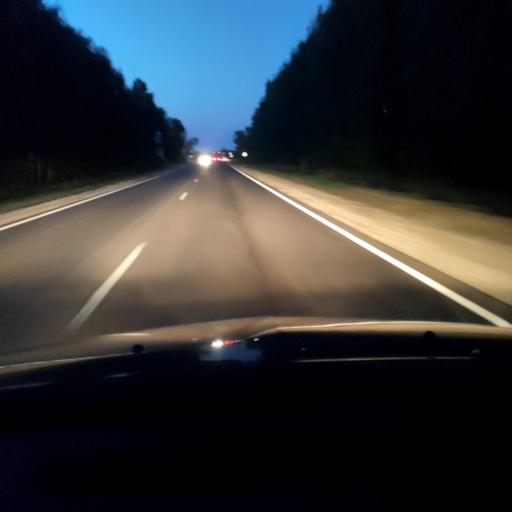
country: RU
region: Voronezj
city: Latnaya
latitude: 51.6448
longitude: 38.7876
